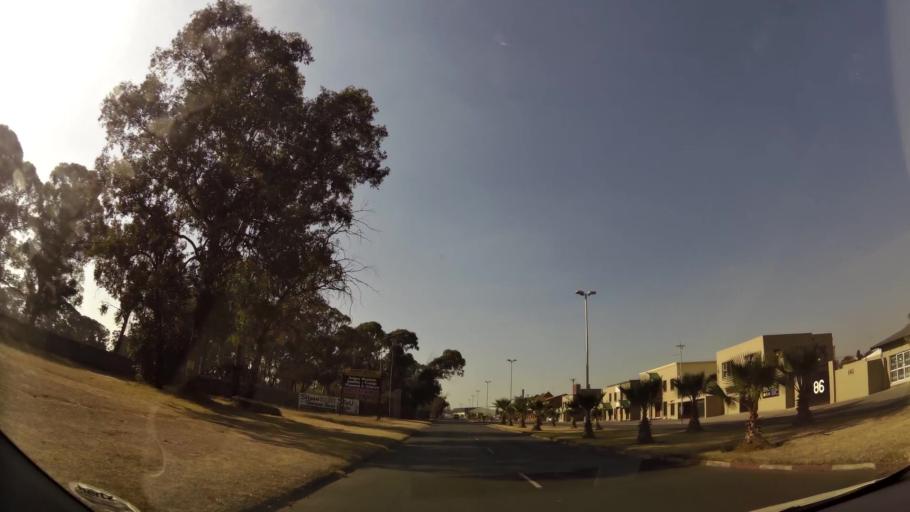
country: ZA
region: Gauteng
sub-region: West Rand District Municipality
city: Randfontein
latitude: -26.1661
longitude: 27.7063
